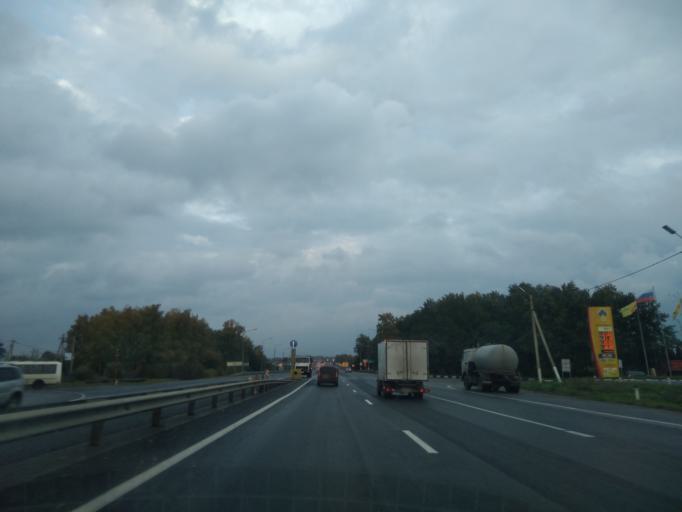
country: RU
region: Lipetsk
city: Syrskoye
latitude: 52.6017
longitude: 39.4117
